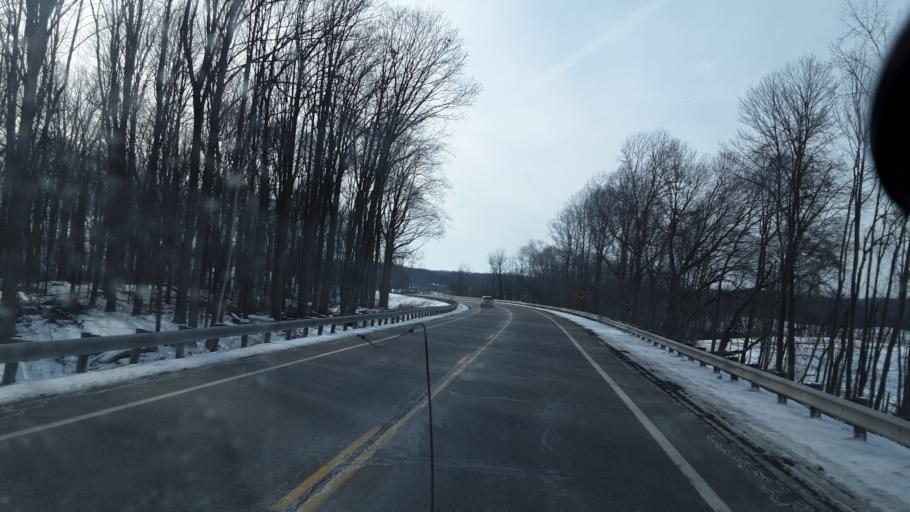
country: US
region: Ohio
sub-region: Stark County
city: Hartville
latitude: 41.0335
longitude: -81.2977
